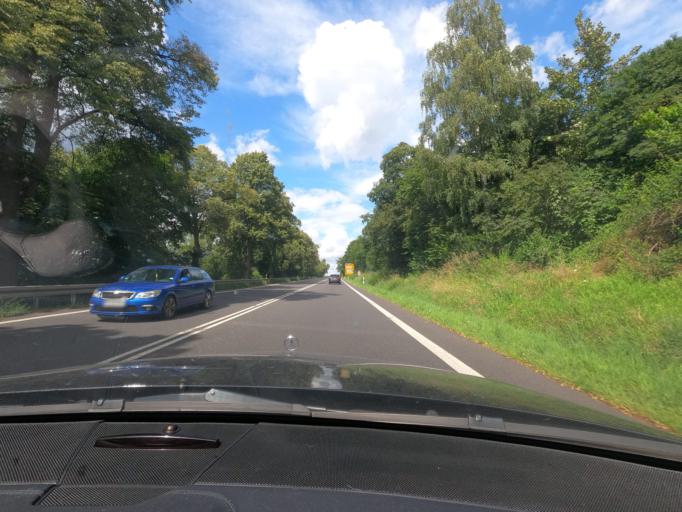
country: DE
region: Hesse
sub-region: Regierungsbezirk Kassel
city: Fulda
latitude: 50.5631
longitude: 9.6922
